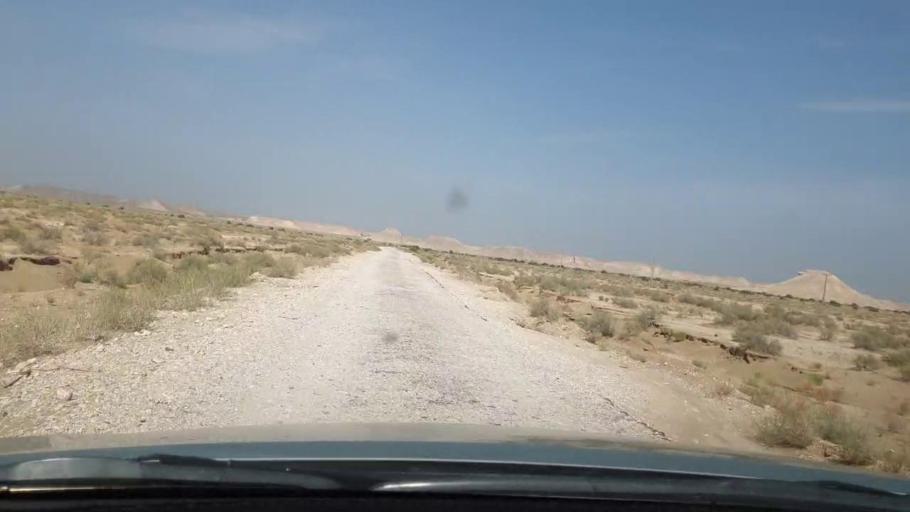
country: PK
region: Sindh
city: Kot Diji
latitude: 27.3274
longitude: 68.8012
